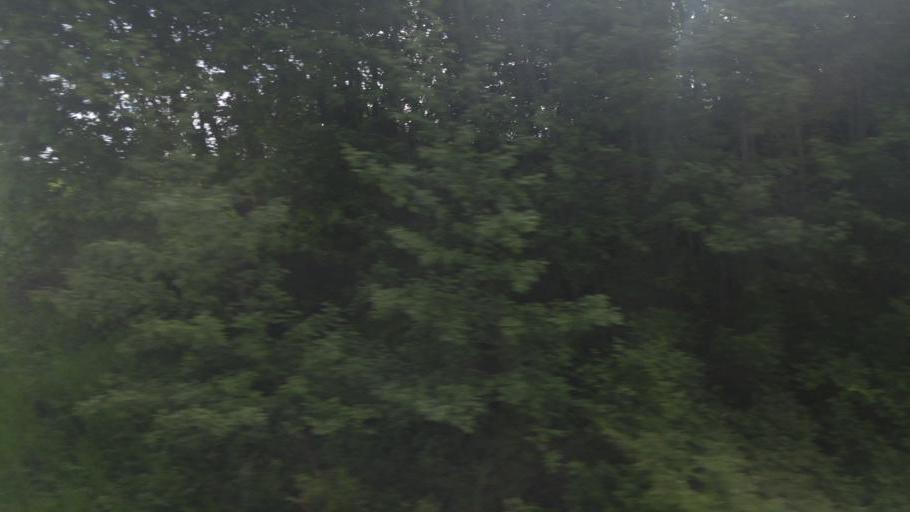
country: NO
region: Sor-Trondelag
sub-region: Melhus
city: Lundamo
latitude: 63.1778
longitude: 10.3074
